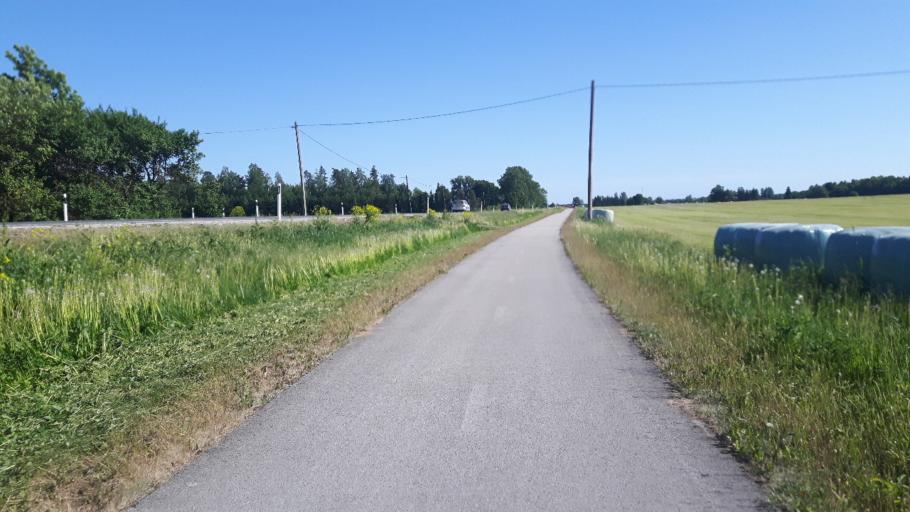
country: EE
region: Raplamaa
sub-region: Kehtna vald
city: Kehtna
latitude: 58.9497
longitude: 24.8756
